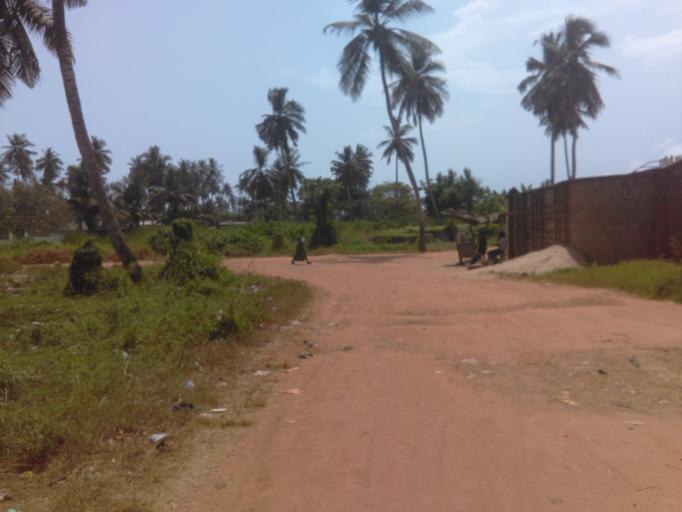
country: GH
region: Central
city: Cape Coast
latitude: 5.1022
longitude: -1.2905
